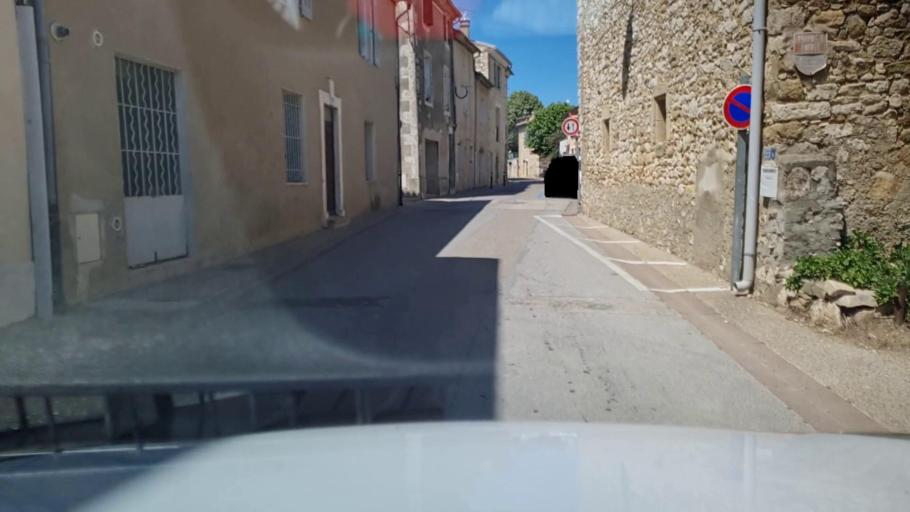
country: FR
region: Languedoc-Roussillon
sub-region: Departement du Gard
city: Saint-Mamert-du-Gard
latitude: 43.8862
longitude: 4.1889
